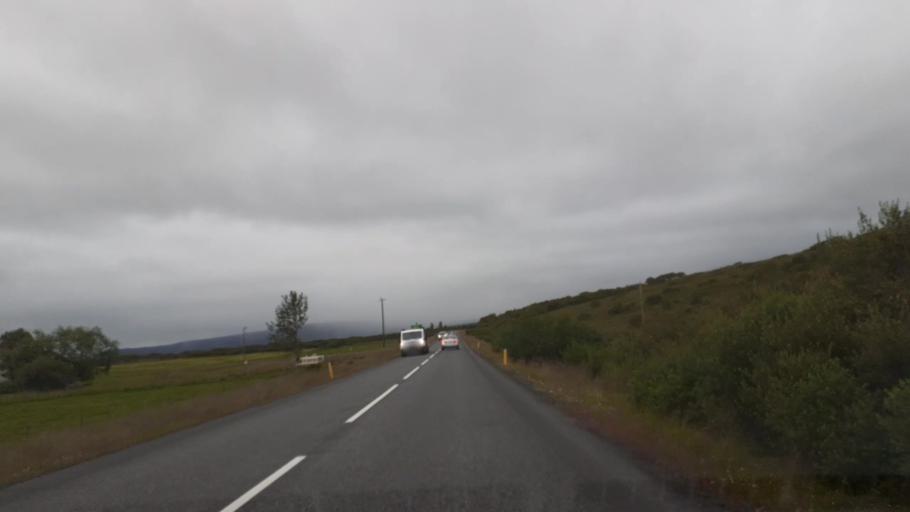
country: IS
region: Northeast
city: Husavik
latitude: 66.0668
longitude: -16.4413
